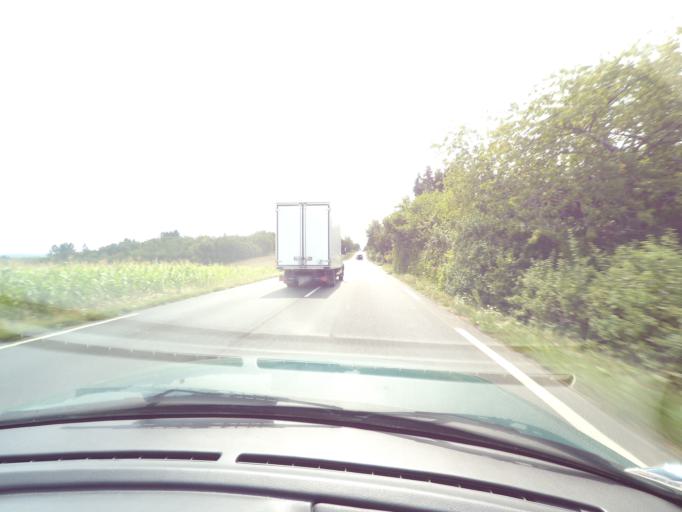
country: FR
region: Limousin
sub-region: Departement de la Haute-Vienne
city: Neuvic-Entier
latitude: 45.7460
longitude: 1.6023
